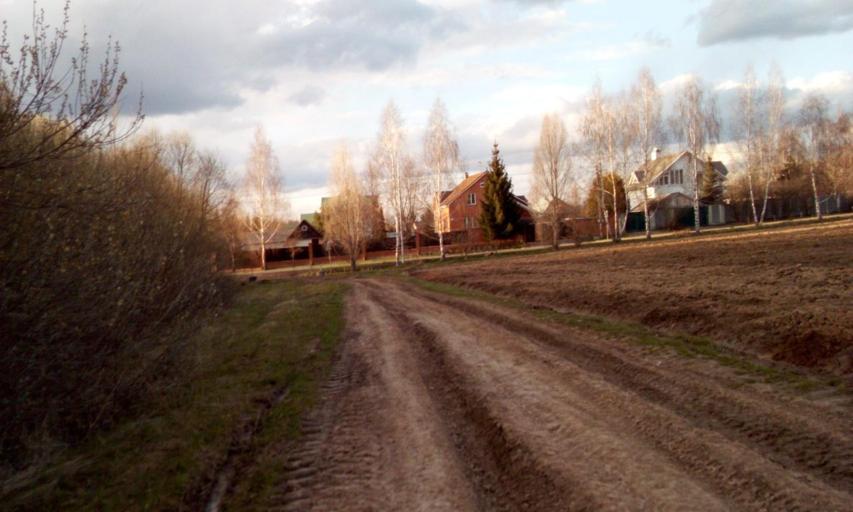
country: RU
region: Moskovskaya
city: Annino
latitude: 55.5504
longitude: 37.2360
